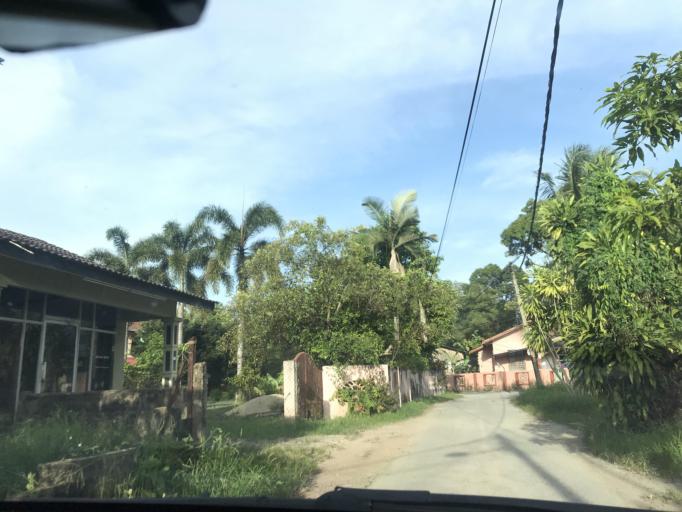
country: MY
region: Kelantan
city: Kota Bharu
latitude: 6.1194
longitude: 102.2218
